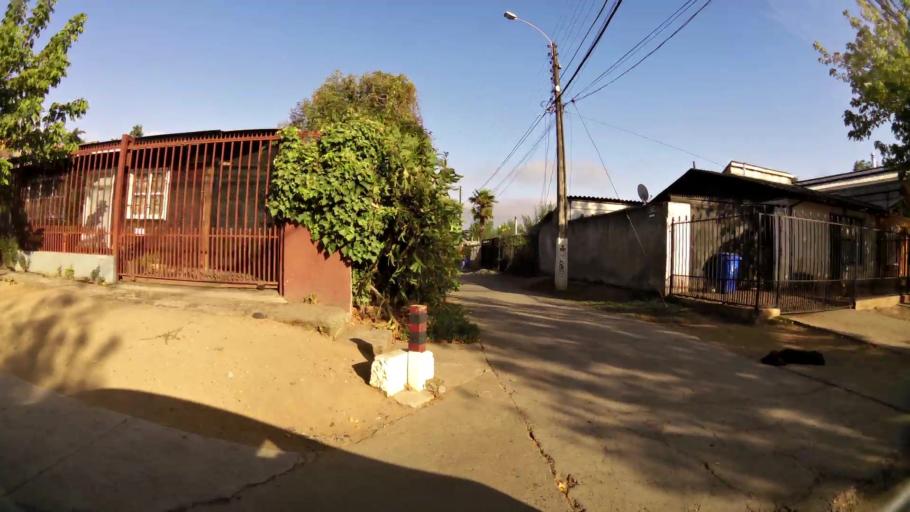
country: CL
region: Maule
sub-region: Provincia de Talca
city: Talca
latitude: -35.4083
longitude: -71.6525
